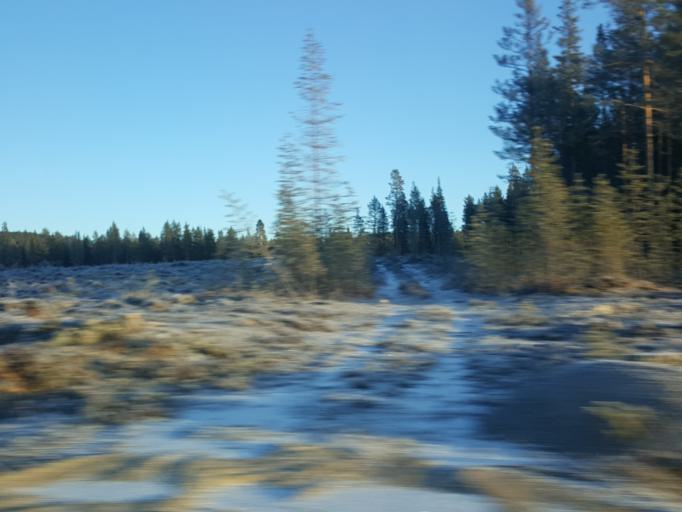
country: SE
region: Jaemtland
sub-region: Harjedalens Kommun
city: Sveg
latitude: 62.2217
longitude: 14.1646
